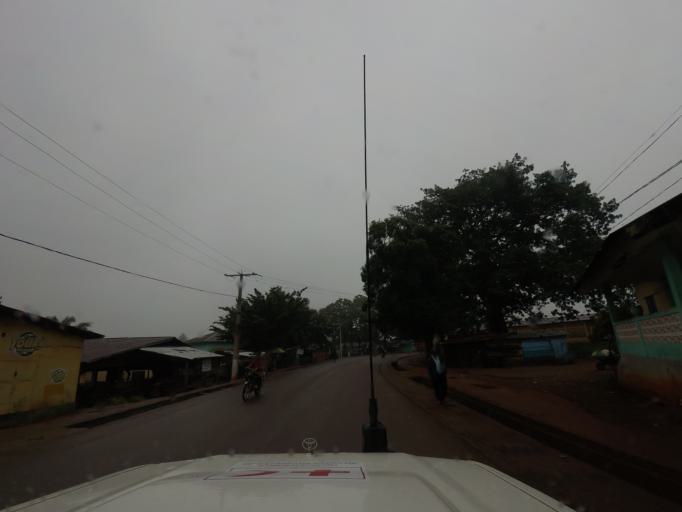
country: GN
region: Nzerekore
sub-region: Nzerekore Prefecture
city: Nzerekore
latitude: 7.7474
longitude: -8.8217
